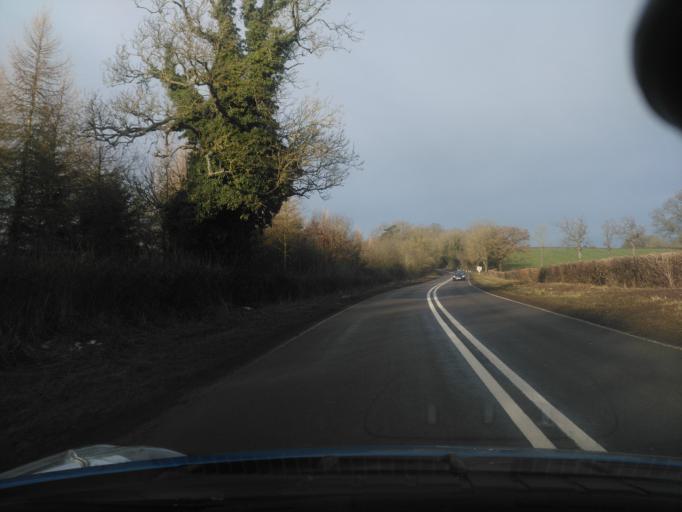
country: GB
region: England
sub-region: Oxfordshire
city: Chipping Norton
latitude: 51.9501
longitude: -1.5888
